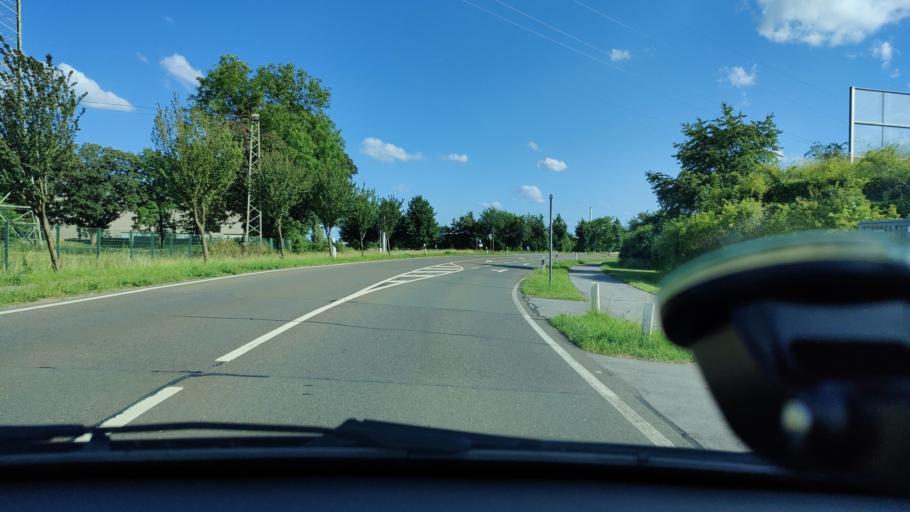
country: DE
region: North Rhine-Westphalia
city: Rheinberg
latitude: 51.5499
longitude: 6.5706
